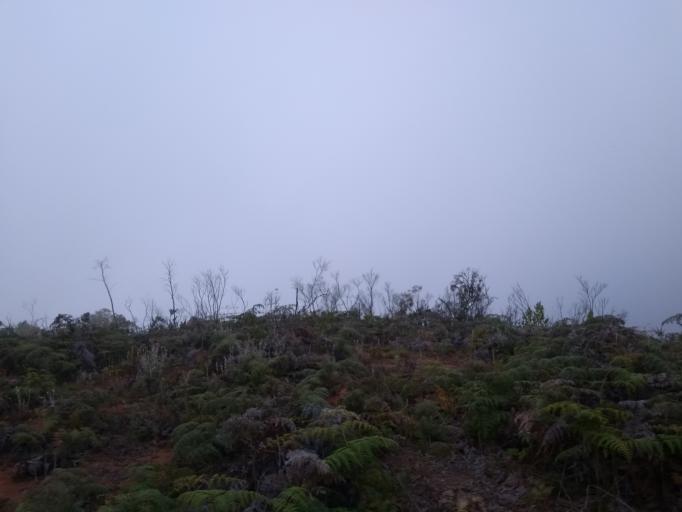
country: CO
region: Cesar
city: Manaure Balcon del Cesar
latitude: 10.2028
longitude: -73.0032
